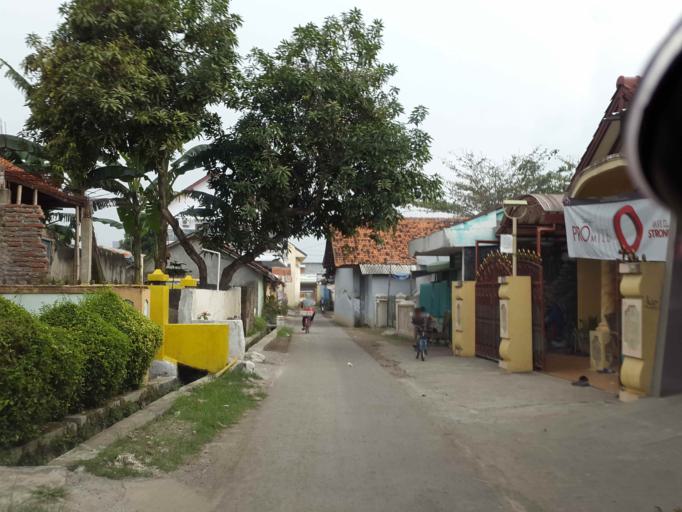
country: ID
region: Central Java
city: Dukuhturi
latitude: -6.9652
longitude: 109.0527
